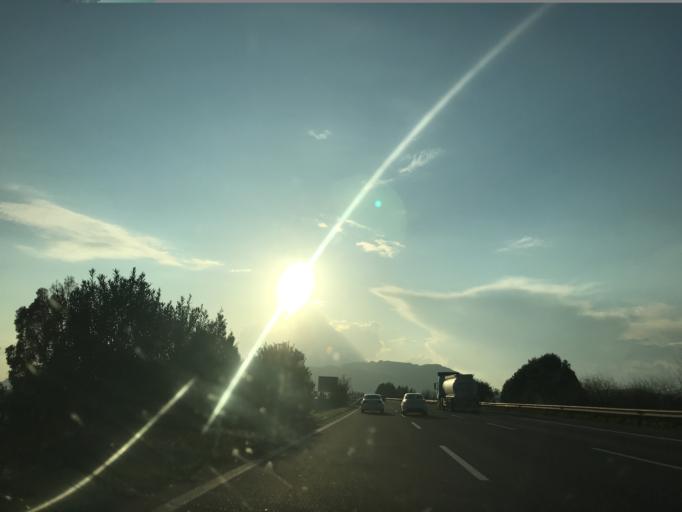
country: TR
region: Adana
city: Ceyhan
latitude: 36.9845
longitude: 35.7997
